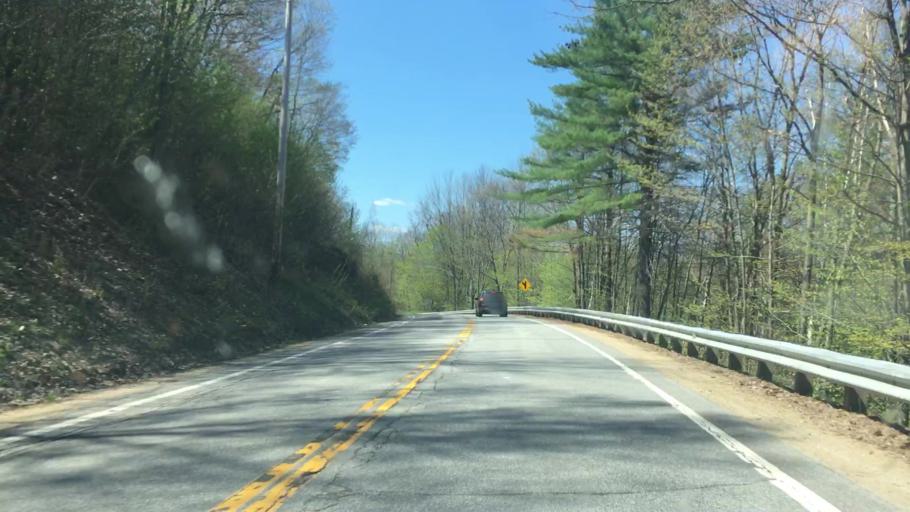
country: US
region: New Hampshire
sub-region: Grafton County
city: Plymouth
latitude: 43.7482
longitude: -71.6839
